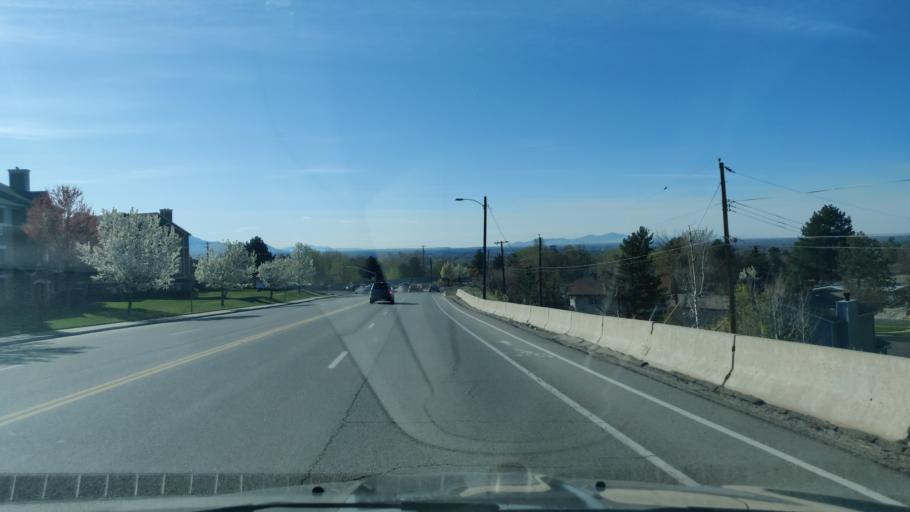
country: US
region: Utah
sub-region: Salt Lake County
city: Little Cottonwood Creek Valley
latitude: 40.6146
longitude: -111.8316
